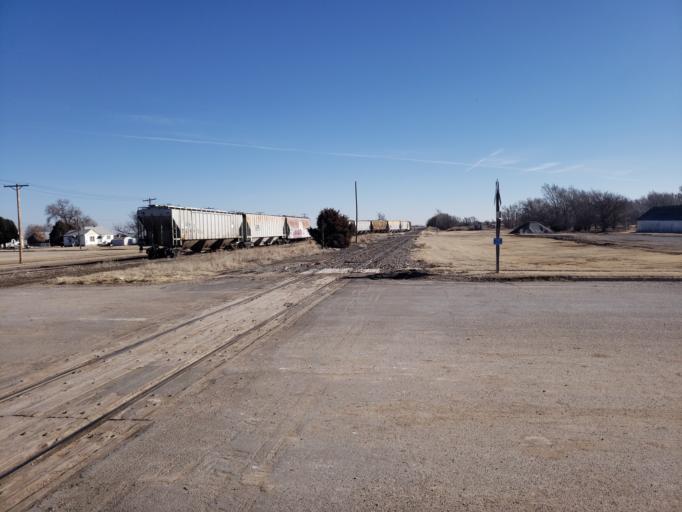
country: US
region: Kansas
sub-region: Ness County
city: Ness City
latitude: 38.4453
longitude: -99.6918
